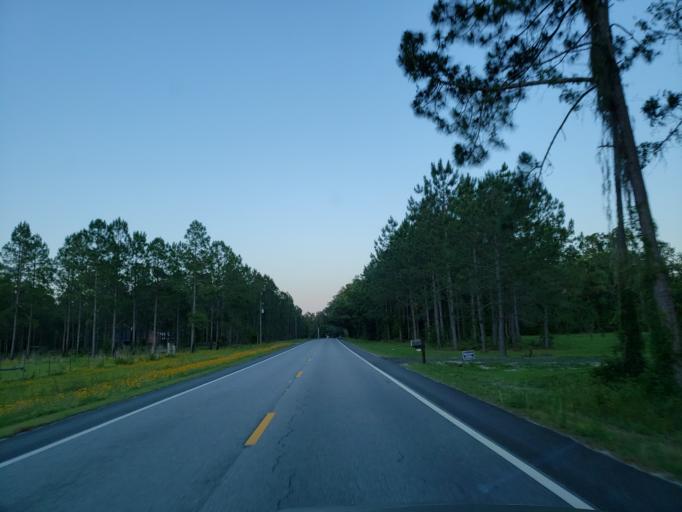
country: US
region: Florida
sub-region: Hamilton County
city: Jasper
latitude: 30.5536
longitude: -83.0701
